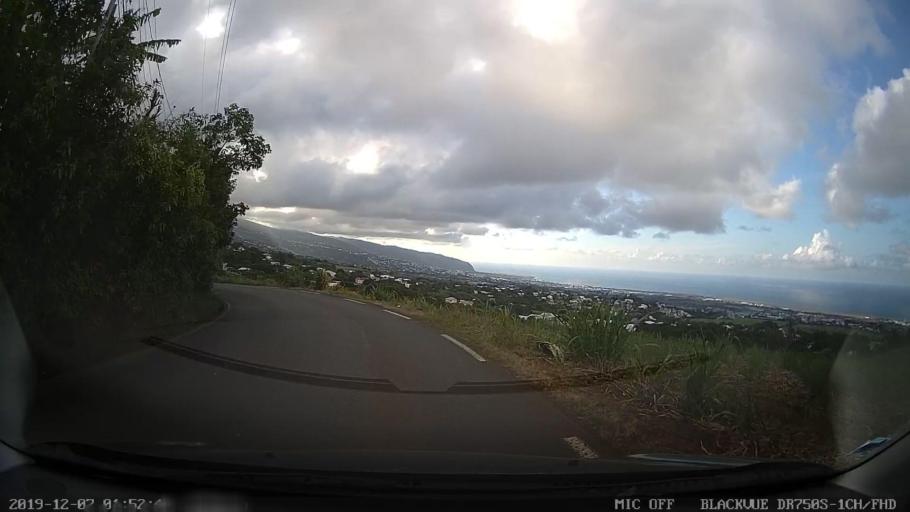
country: RE
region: Reunion
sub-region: Reunion
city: Sainte-Marie
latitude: -20.9389
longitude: 55.5343
